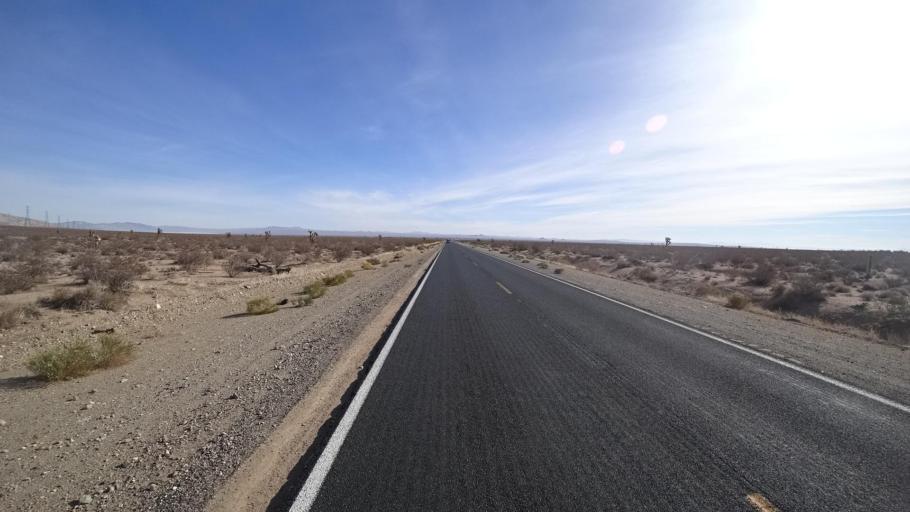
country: US
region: California
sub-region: Kern County
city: Mojave
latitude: 35.1249
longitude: -118.1574
